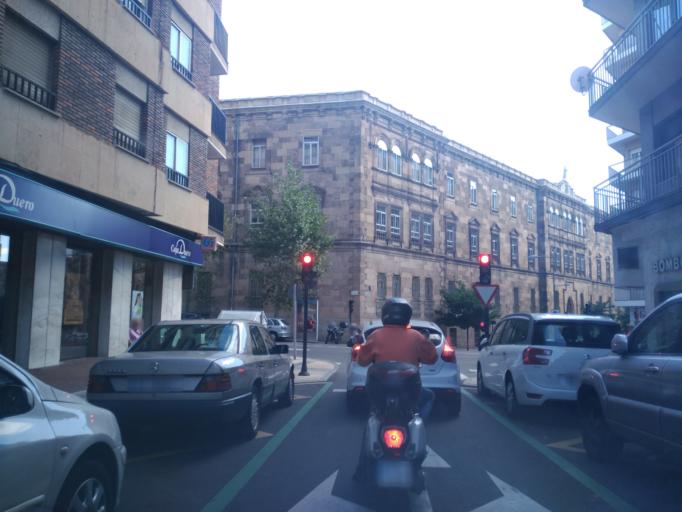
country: ES
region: Castille and Leon
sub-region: Provincia de Salamanca
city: Salamanca
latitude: 40.9706
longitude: -5.6589
